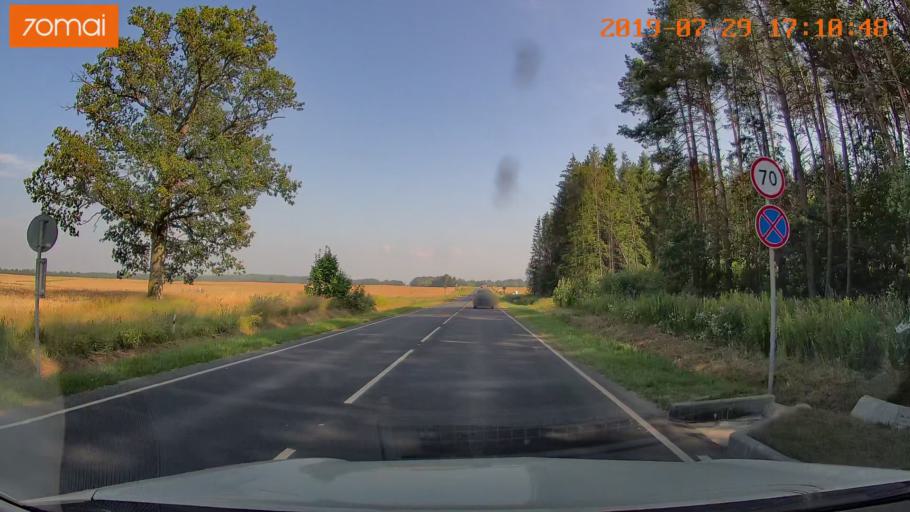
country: RU
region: Kaliningrad
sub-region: Gorod Kaliningrad
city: Kaliningrad
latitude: 54.7996
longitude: 20.3727
